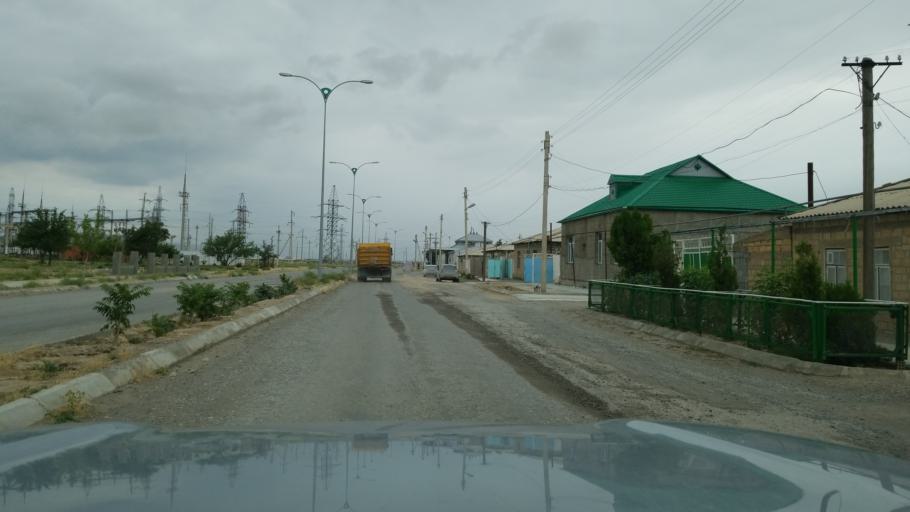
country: TM
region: Balkan
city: Serdar
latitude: 38.9713
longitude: 56.2573
